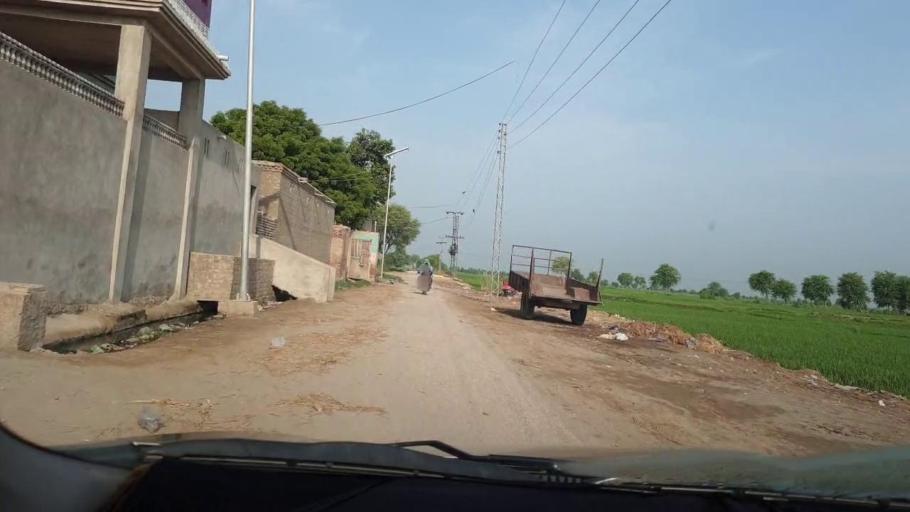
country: PK
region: Sindh
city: Goth Garelo
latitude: 27.4815
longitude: 68.0853
